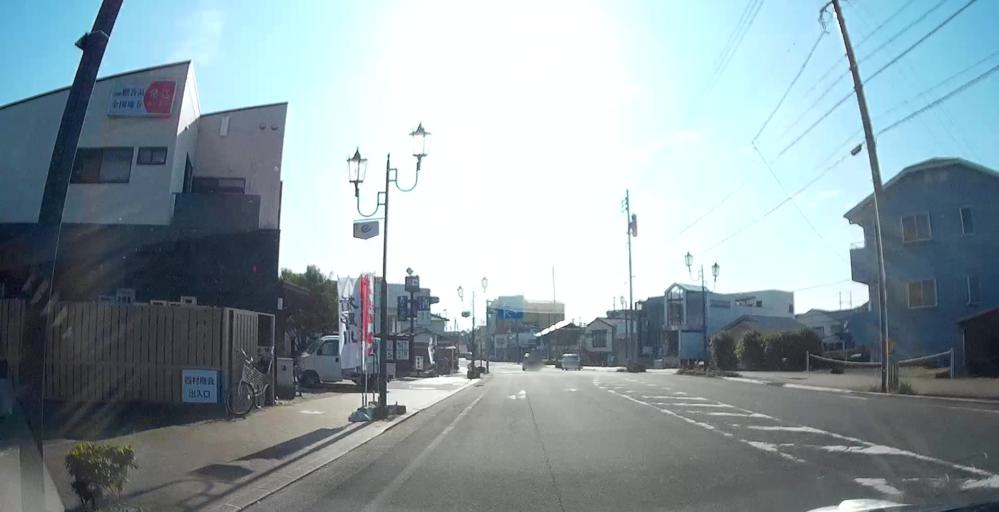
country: JP
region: Kumamoto
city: Kumamoto
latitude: 32.7454
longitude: 130.6824
